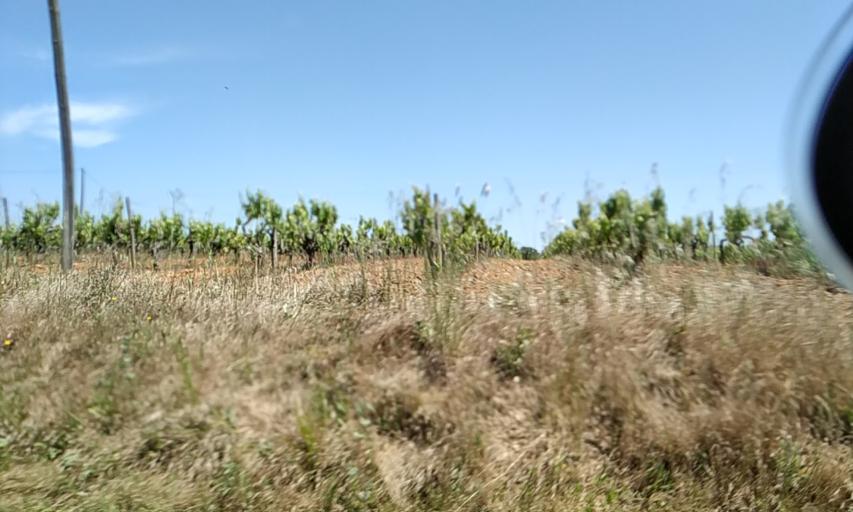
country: PT
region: Santarem
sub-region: Benavente
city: Poceirao
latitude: 38.6632
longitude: -8.7383
